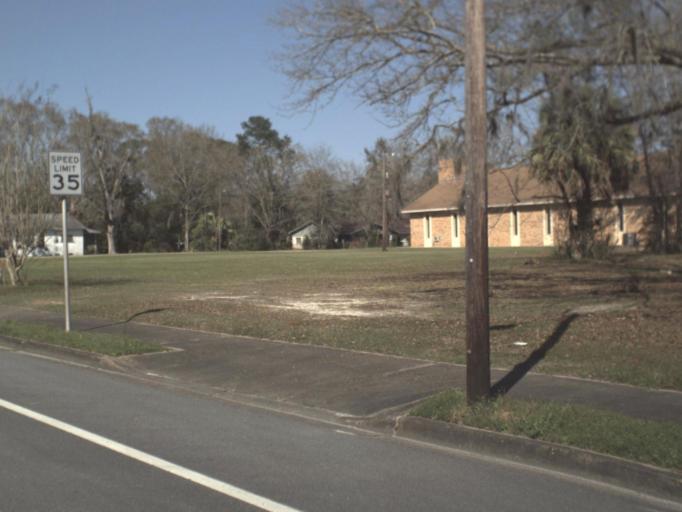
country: US
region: Florida
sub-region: Gulf County
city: Wewahitchka
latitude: 30.1026
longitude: -85.2007
